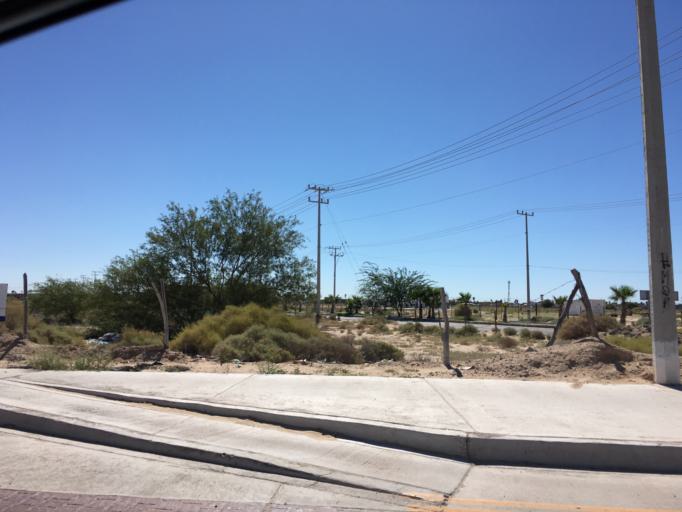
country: MX
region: Sonora
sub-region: Puerto Penasco
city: Puerto Penasco
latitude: 31.3339
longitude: -113.5285
